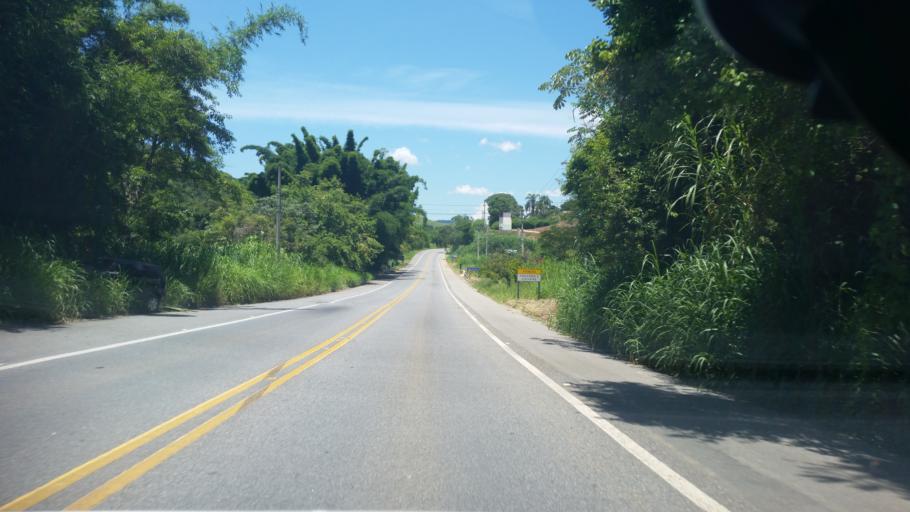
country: BR
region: Sao Paulo
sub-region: Taubate
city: Taubate
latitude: -23.1173
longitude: -45.5179
